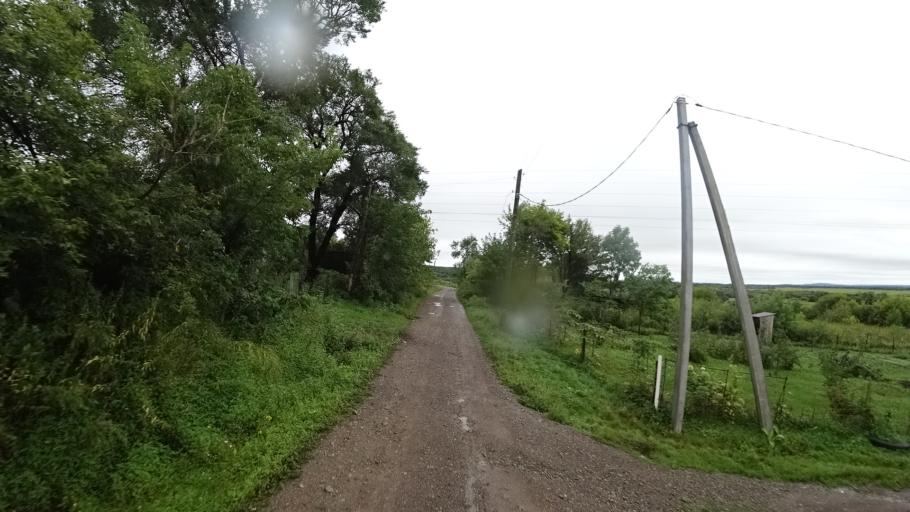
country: RU
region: Primorskiy
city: Monastyrishche
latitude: 44.2628
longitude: 132.4049
